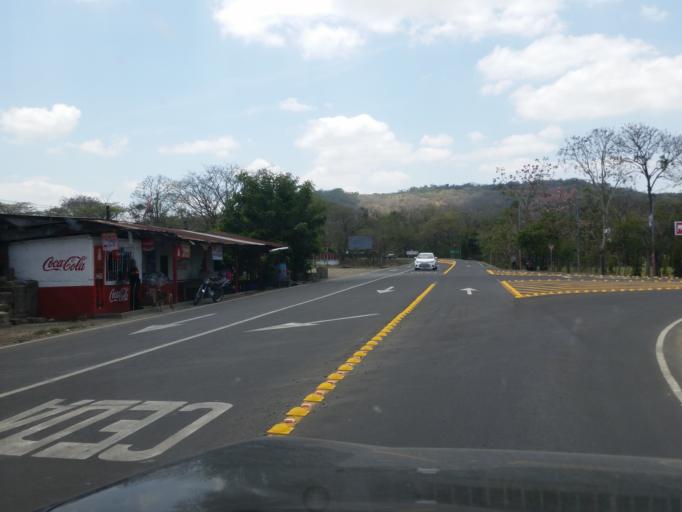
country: NI
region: Boaco
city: Boaco
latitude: 12.4846
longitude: -85.6030
